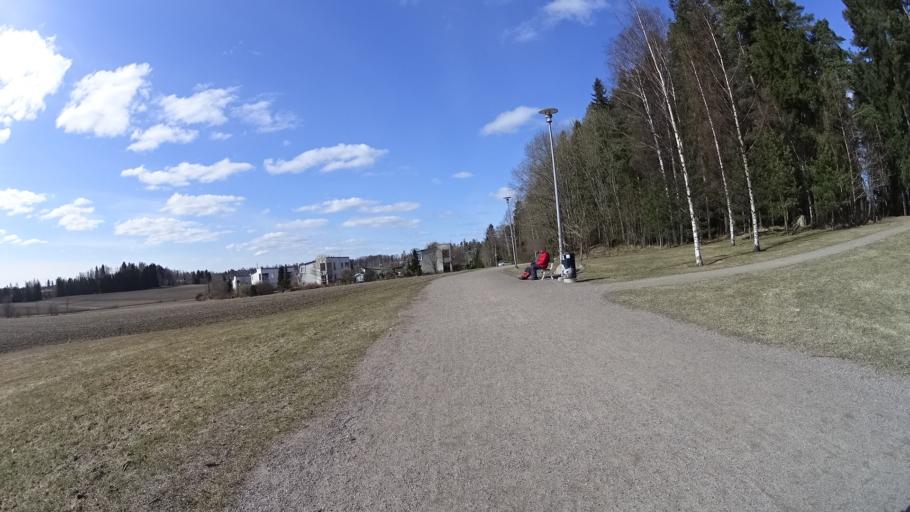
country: FI
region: Uusimaa
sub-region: Helsinki
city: Kauniainen
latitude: 60.2499
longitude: 24.7208
